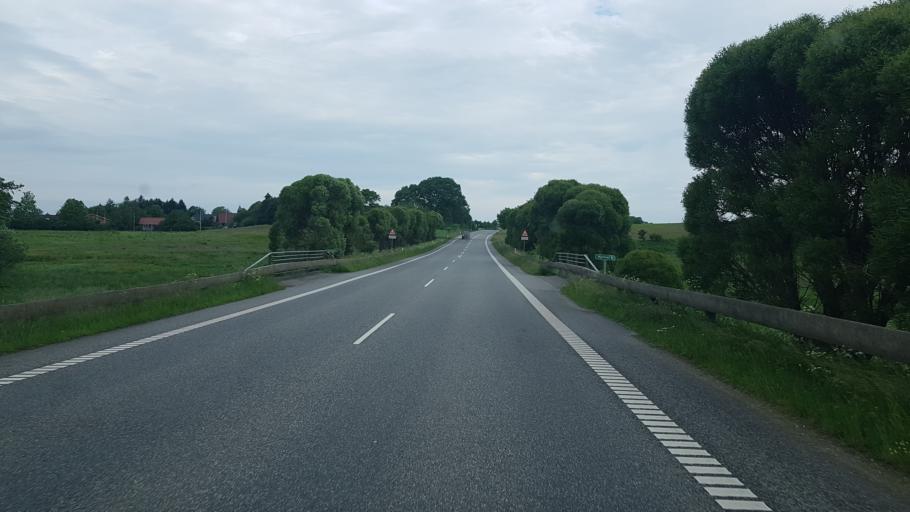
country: DK
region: South Denmark
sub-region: Vejen Kommune
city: Rodding
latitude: 55.3891
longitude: 9.0443
